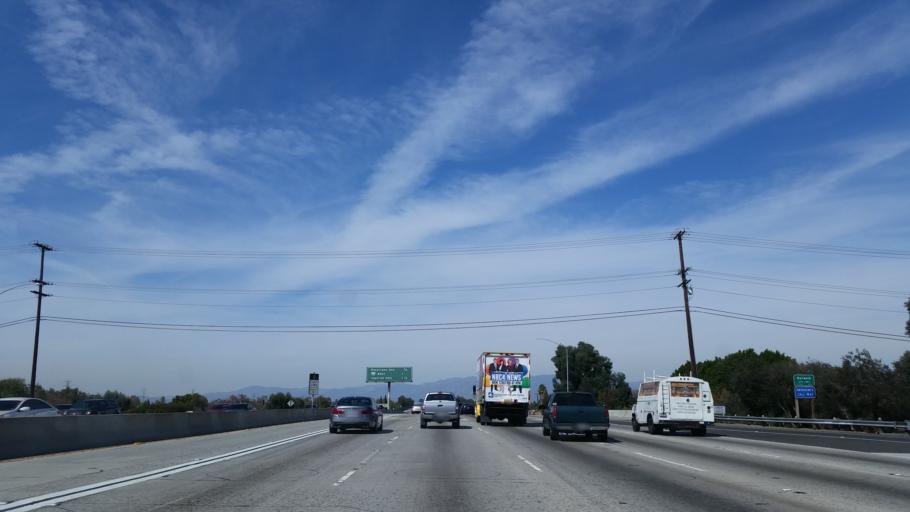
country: US
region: California
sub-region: Los Angeles County
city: Bellflower
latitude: 33.8866
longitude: -118.1042
